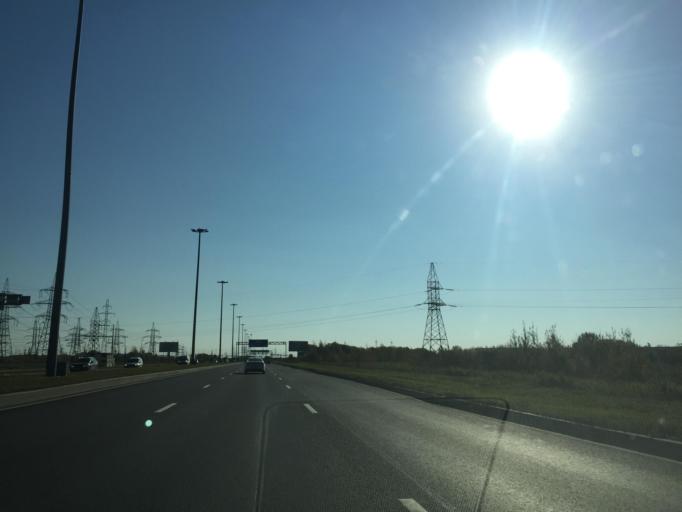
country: RU
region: St.-Petersburg
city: Petro-Slavyanka
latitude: 59.7534
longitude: 30.5233
